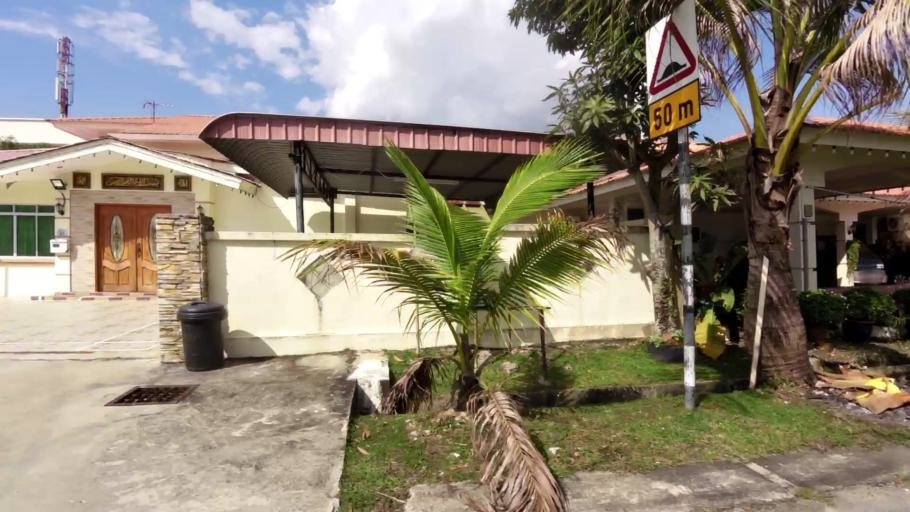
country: BN
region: Brunei and Muara
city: Bandar Seri Begawan
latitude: 4.9531
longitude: 114.9536
